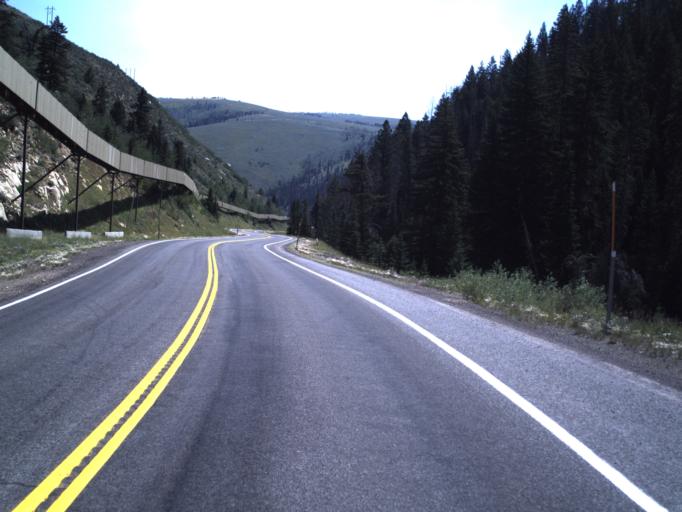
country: US
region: Utah
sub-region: Sanpete County
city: Fairview
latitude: 39.6822
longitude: -111.1756
